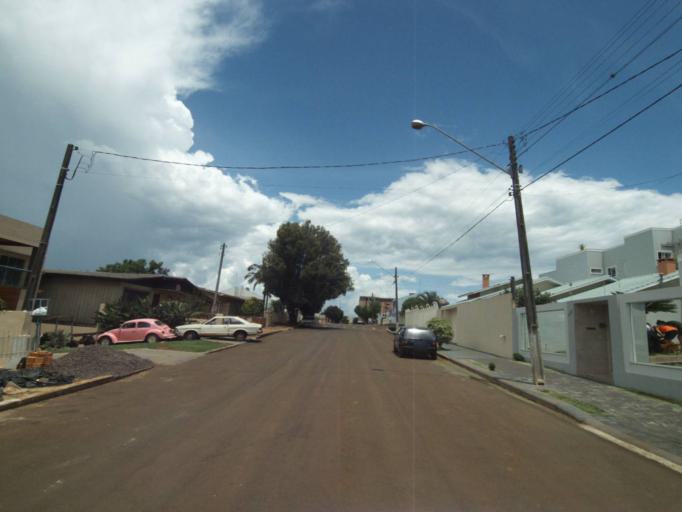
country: BR
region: Parana
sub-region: Guaraniacu
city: Guaraniacu
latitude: -25.0966
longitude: -52.8712
